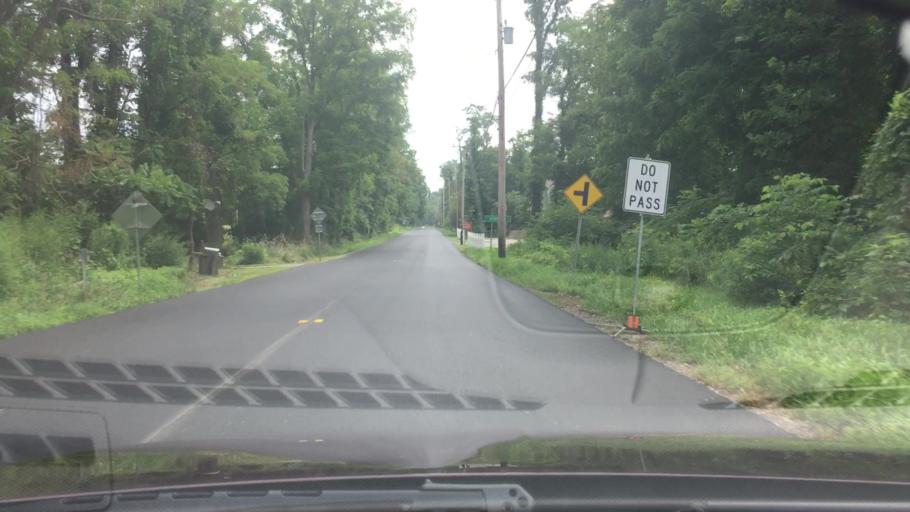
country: US
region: New York
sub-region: Dutchess County
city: Hillside Lake
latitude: 41.5683
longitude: -73.7584
